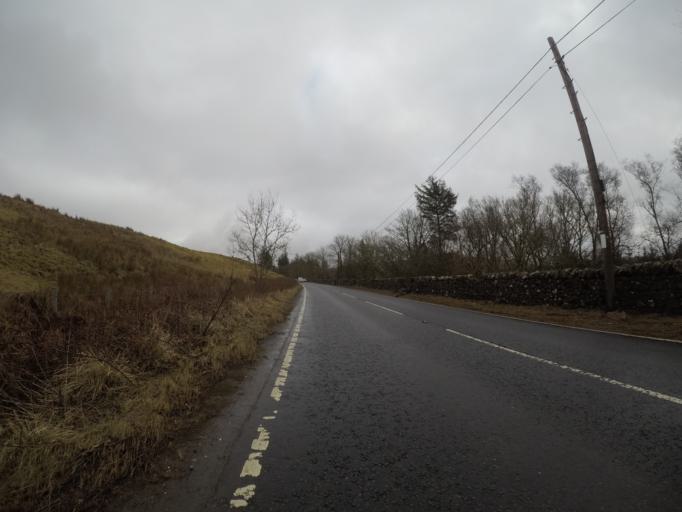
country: GB
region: Scotland
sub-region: North Ayrshire
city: Fairlie
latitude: 55.7757
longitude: -4.8383
